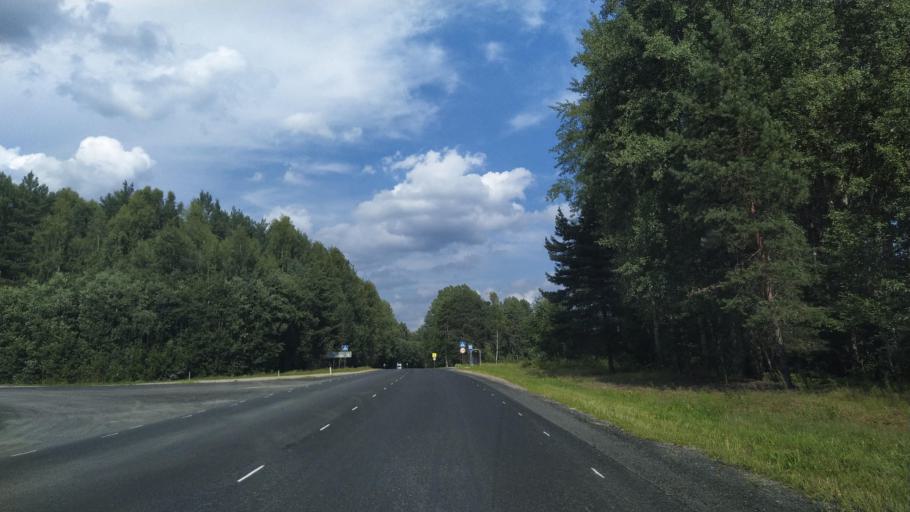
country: RU
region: Pskov
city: Porkhov
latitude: 57.7373
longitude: 29.4161
